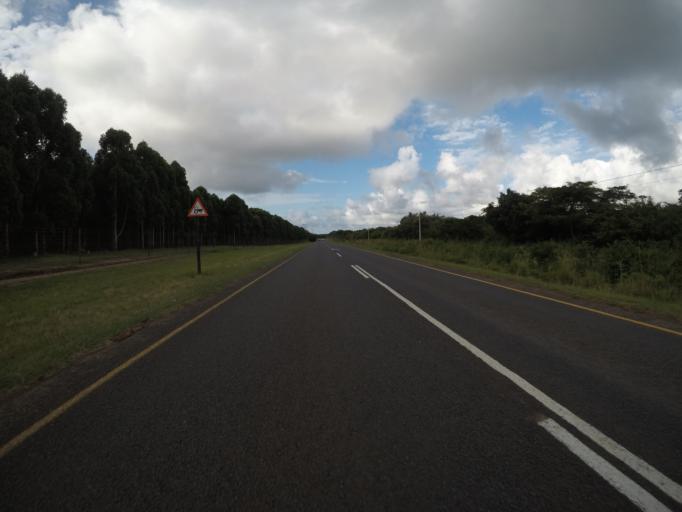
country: ZA
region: KwaZulu-Natal
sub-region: uMkhanyakude District Municipality
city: Mtubatuba
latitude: -28.3767
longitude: 32.2508
